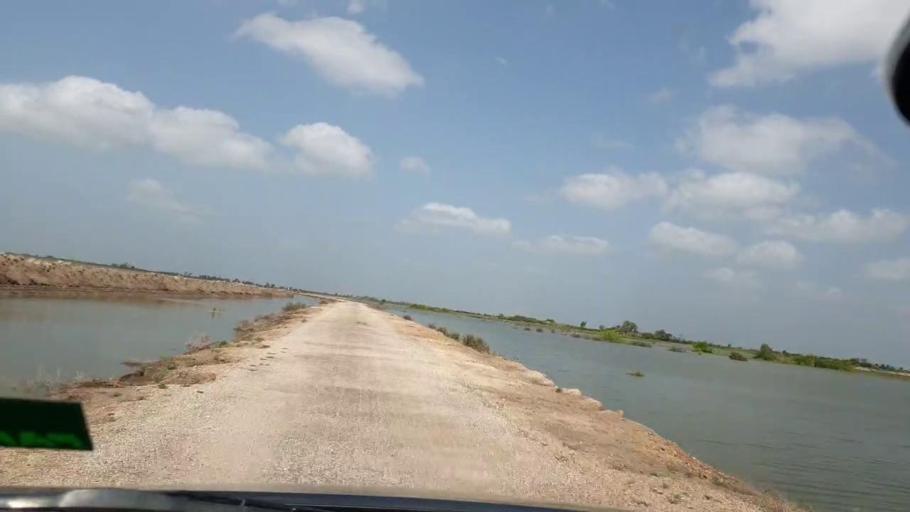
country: PK
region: Sindh
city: Kadhan
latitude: 24.5913
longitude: 69.1352
